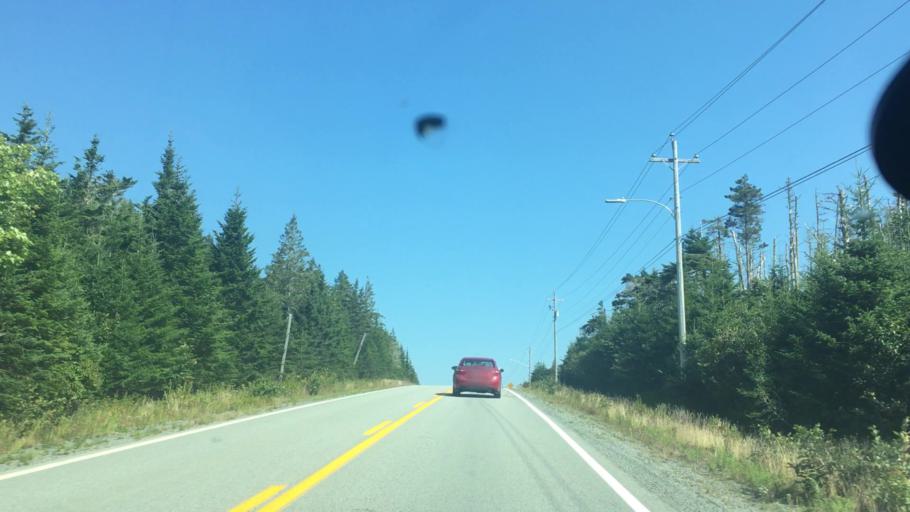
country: CA
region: Nova Scotia
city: Antigonish
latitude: 44.9380
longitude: -62.2690
